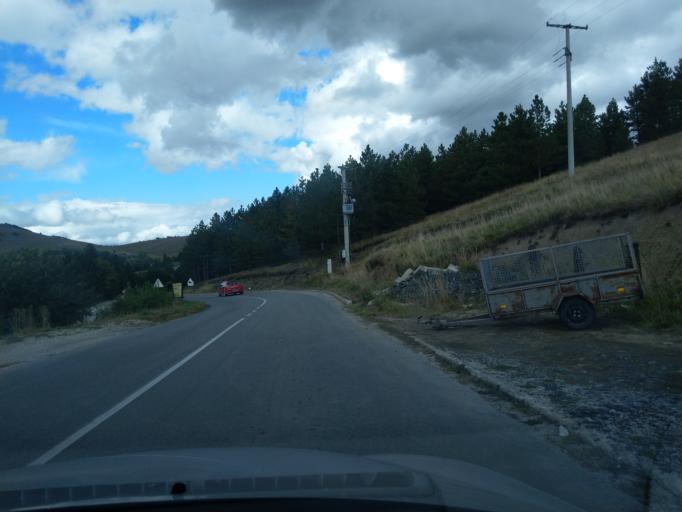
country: RS
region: Central Serbia
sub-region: Zlatiborski Okrug
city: Cajetina
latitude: 43.7167
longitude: 19.7620
